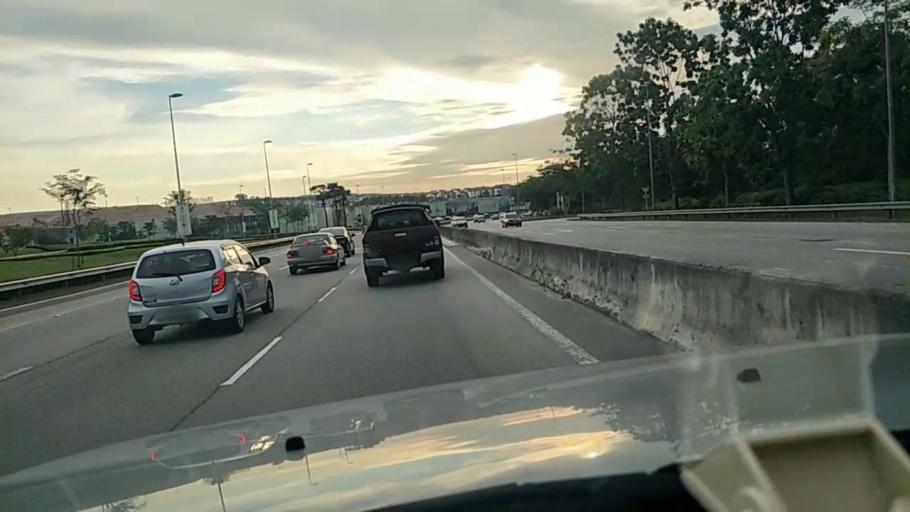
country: MY
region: Selangor
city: Shah Alam
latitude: 3.0995
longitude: 101.4785
